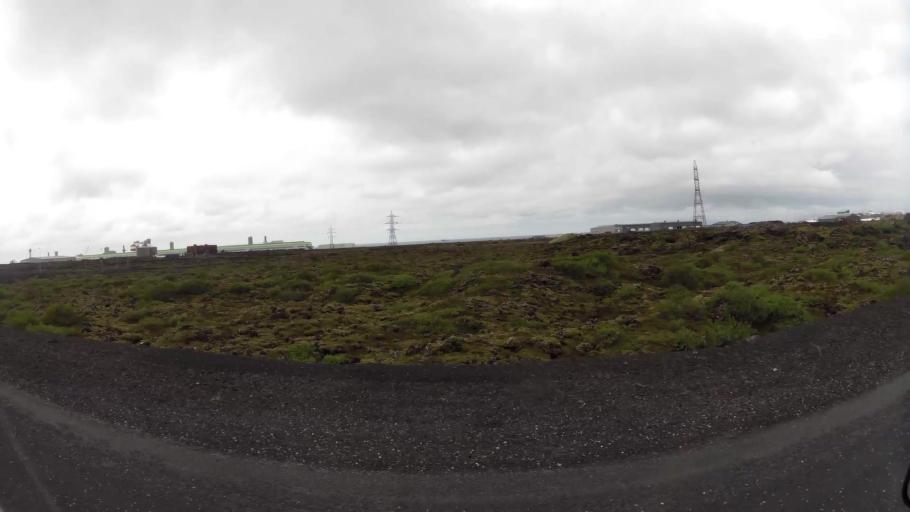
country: IS
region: Capital Region
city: Alftanes
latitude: 64.0412
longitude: -22.0060
